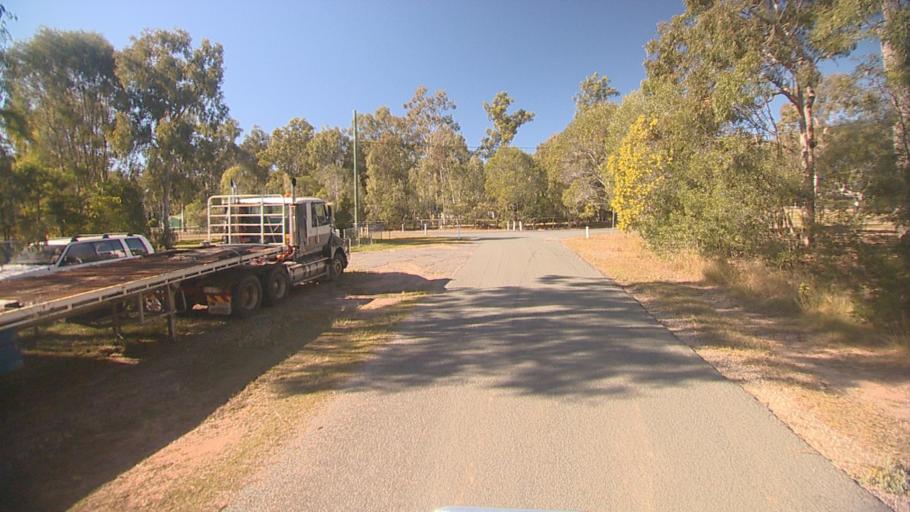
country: AU
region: Queensland
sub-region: Logan
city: Chambers Flat
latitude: -27.7478
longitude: 153.0514
